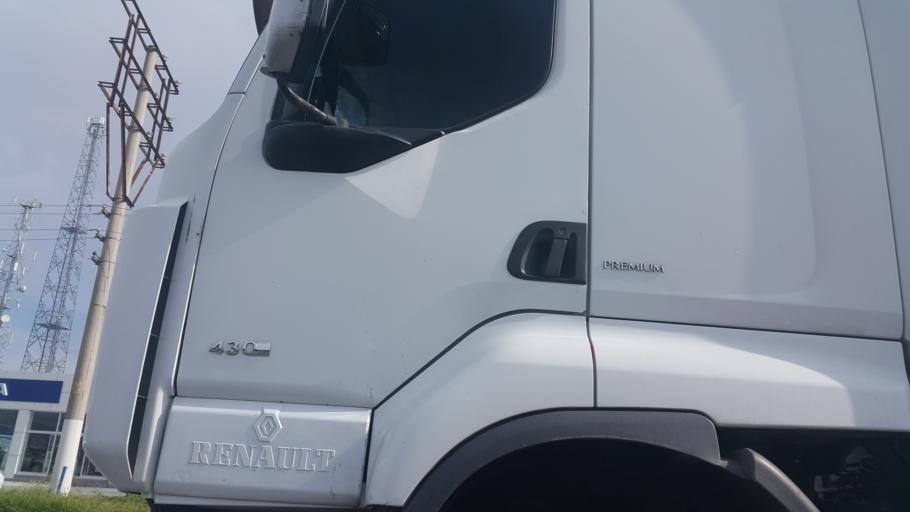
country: TR
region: Mersin
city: Tarsus
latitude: 36.9040
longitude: 34.8734
